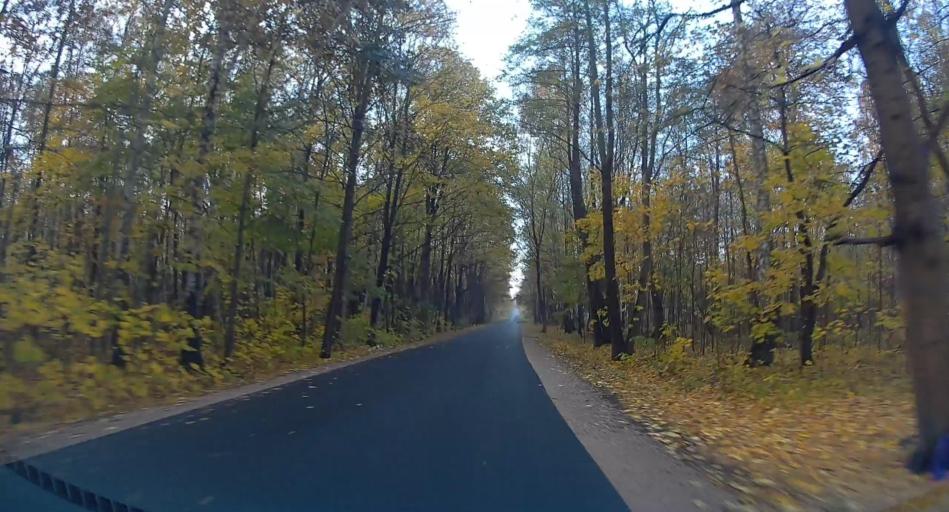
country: PL
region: Masovian Voivodeship
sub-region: Powiat zyrardowski
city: Puszcza Marianska
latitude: 51.9423
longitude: 20.3699
